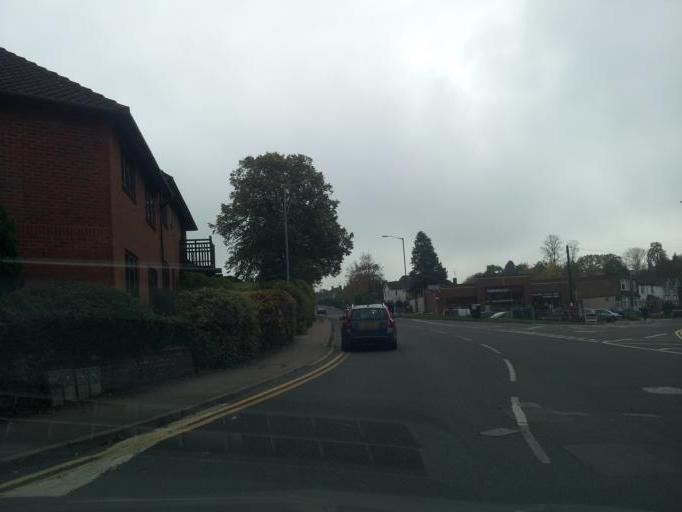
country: GB
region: England
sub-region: Buckinghamshire
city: Buckingham
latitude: 51.9977
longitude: -0.9855
